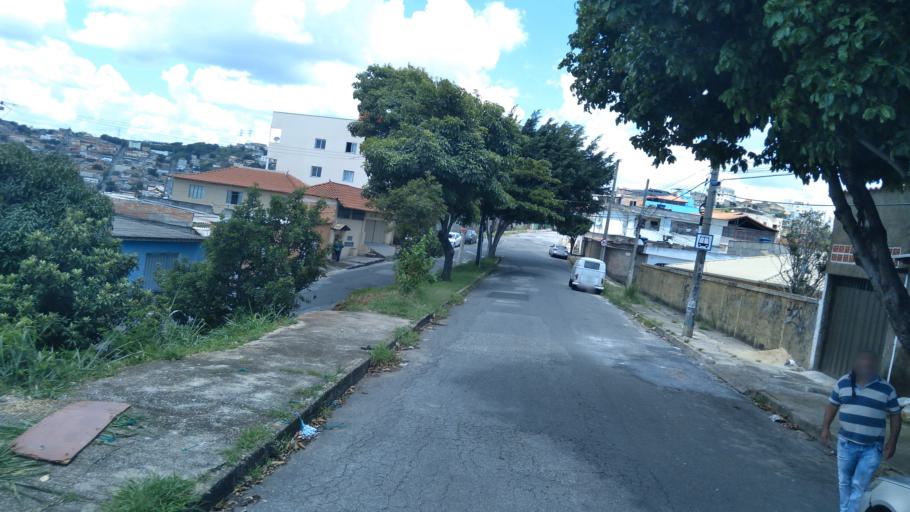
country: BR
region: Minas Gerais
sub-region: Belo Horizonte
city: Belo Horizonte
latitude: -19.8644
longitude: -43.9146
